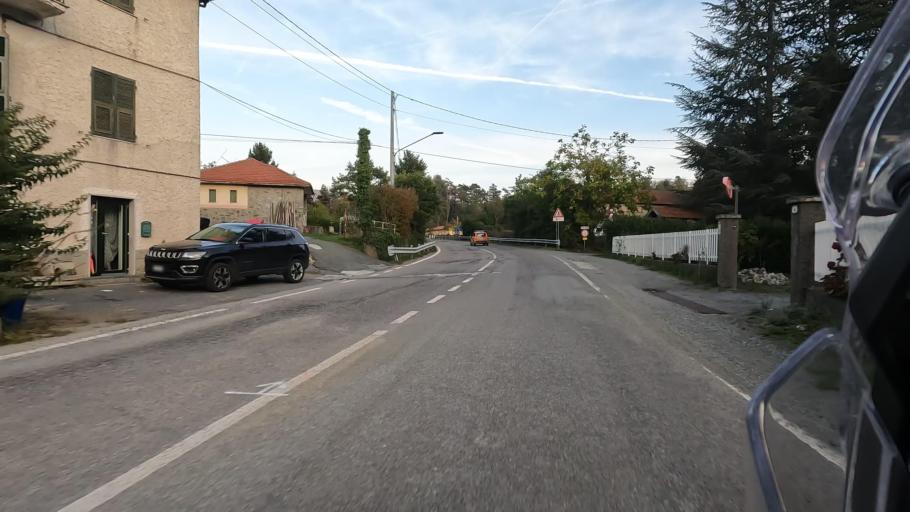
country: IT
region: Liguria
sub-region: Provincia di Savona
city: Osteria dei Cacciatori-Stella
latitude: 44.4292
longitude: 8.4693
